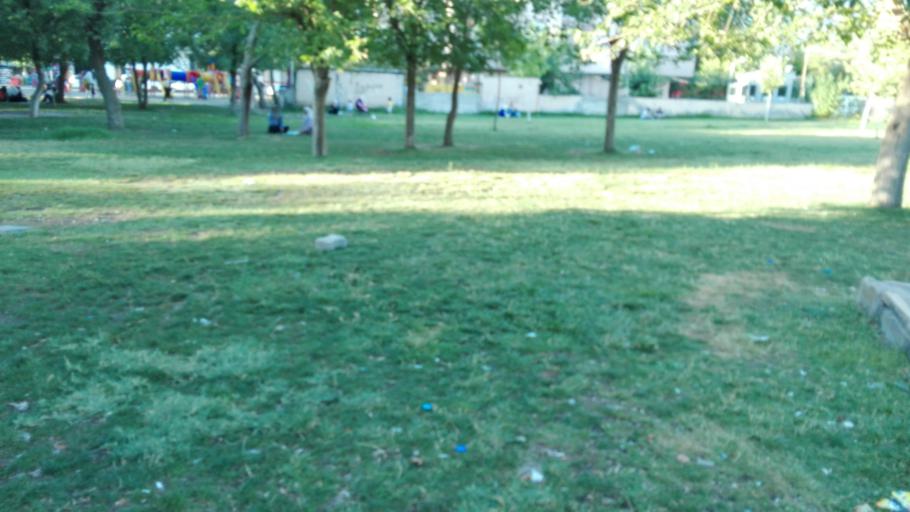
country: TR
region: Batman
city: Batman
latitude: 37.8954
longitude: 41.1324
